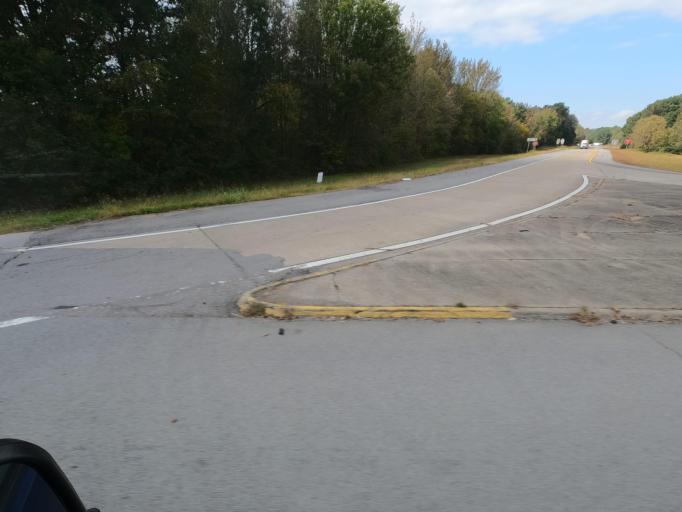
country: US
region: Tennessee
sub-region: Cheatham County
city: Pleasant View
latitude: 36.4484
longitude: -87.1005
